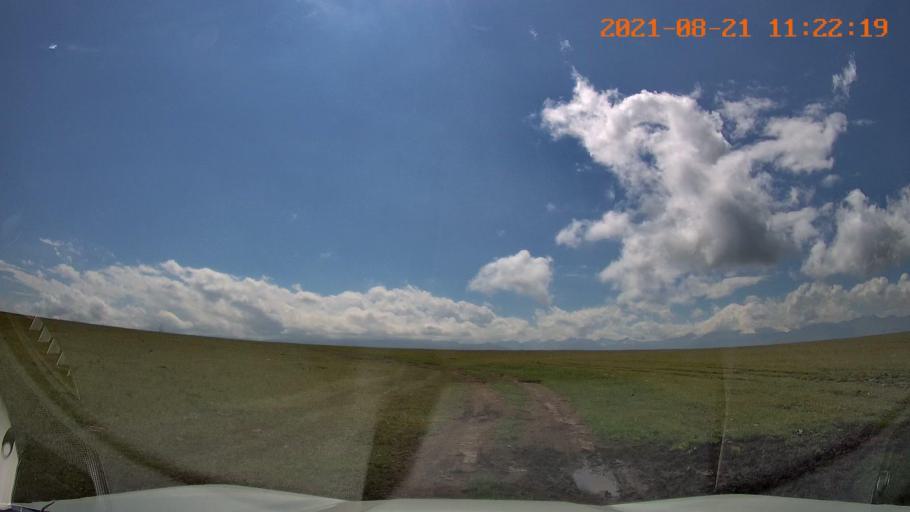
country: RU
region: Stavropol'skiy
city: Kislovodsk
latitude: 43.6155
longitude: 42.5920
